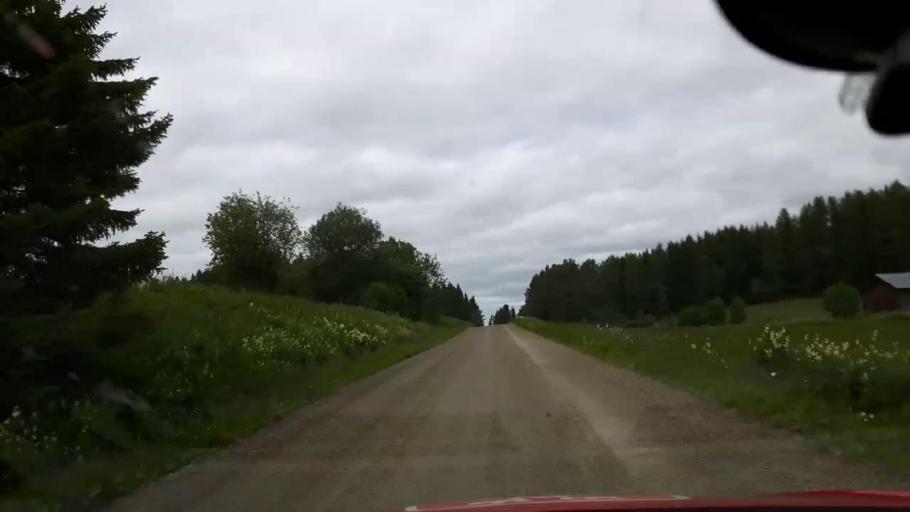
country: SE
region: Jaemtland
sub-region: OEstersunds Kommun
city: Brunflo
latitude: 62.9208
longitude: 15.0137
